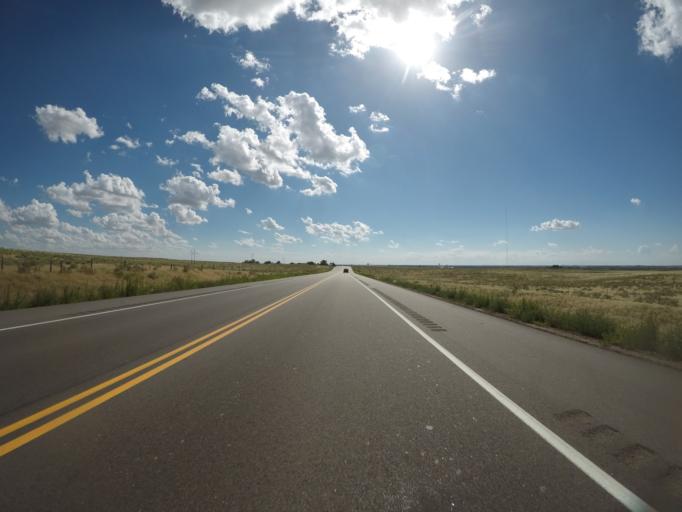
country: US
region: Colorado
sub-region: Logan County
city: Sterling
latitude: 40.6269
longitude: -103.1527
